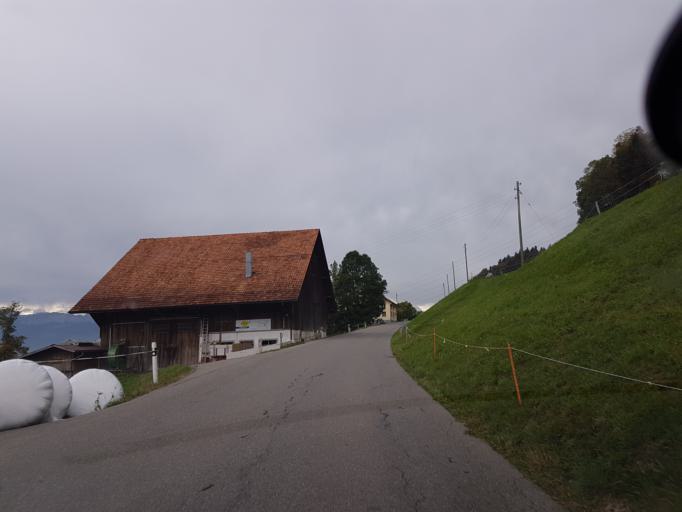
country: CH
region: Saint Gallen
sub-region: Wahlkreis See-Gaster
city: Goldingen
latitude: 47.2740
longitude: 8.9726
